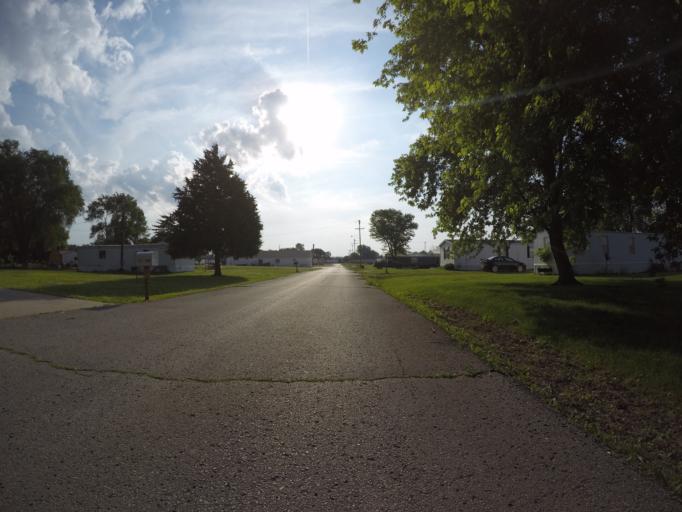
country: US
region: Kansas
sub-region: Doniphan County
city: Elwood
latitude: 39.7519
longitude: -94.8711
